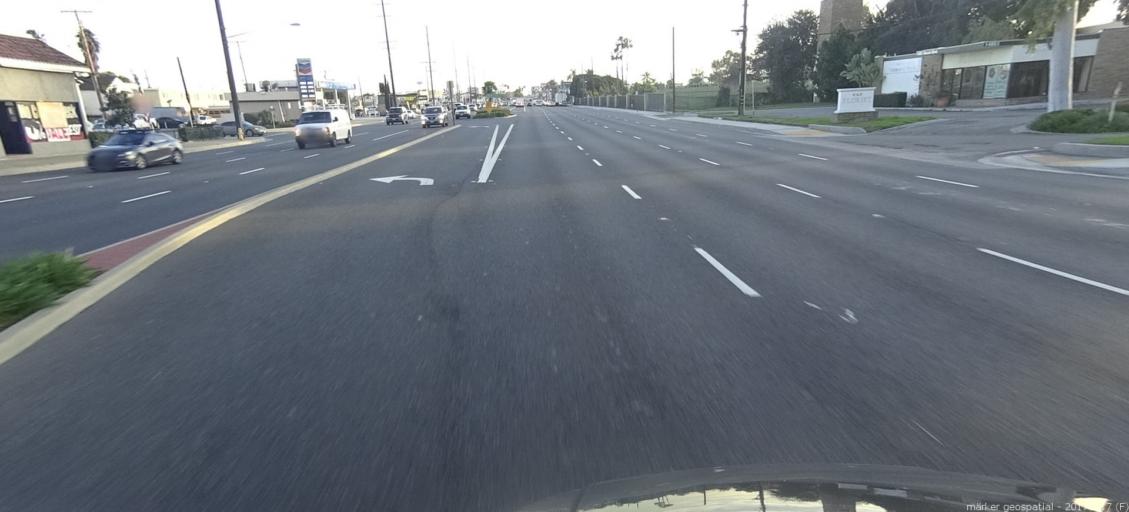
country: US
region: California
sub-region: Orange County
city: Midway City
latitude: 33.7473
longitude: -117.9896
